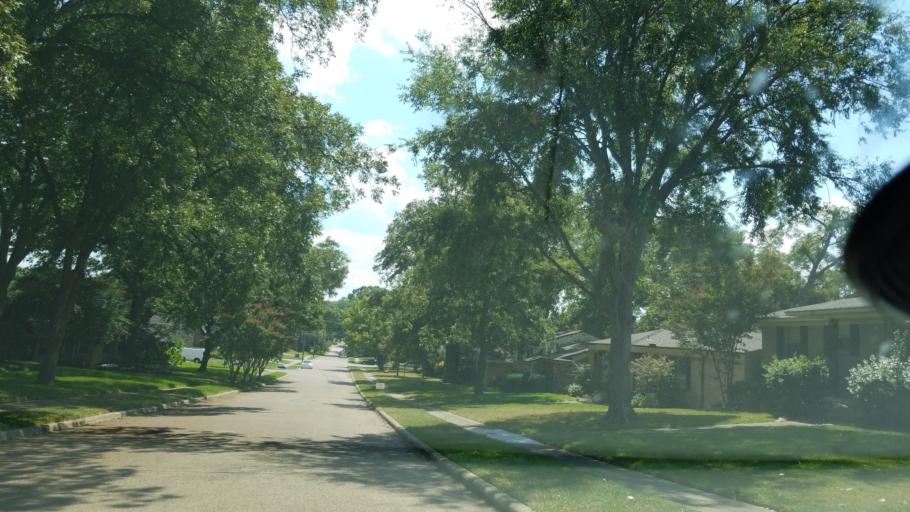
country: US
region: Texas
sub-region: Dallas County
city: Richardson
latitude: 32.8805
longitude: -96.7150
